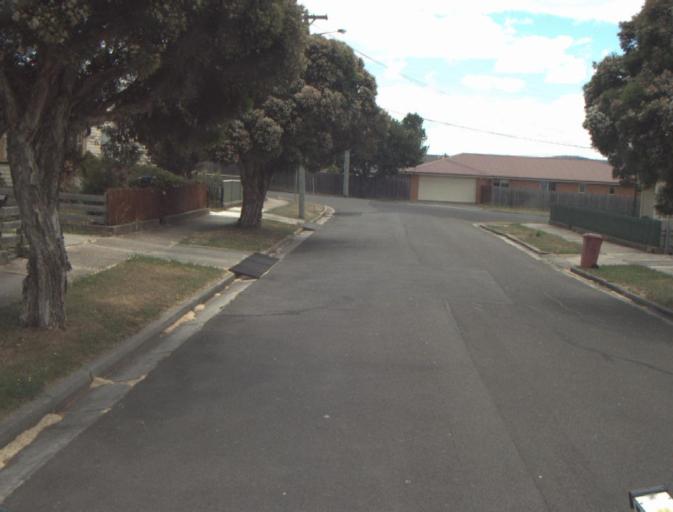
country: AU
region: Tasmania
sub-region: Launceston
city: Newstead
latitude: -41.4376
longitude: 147.1609
